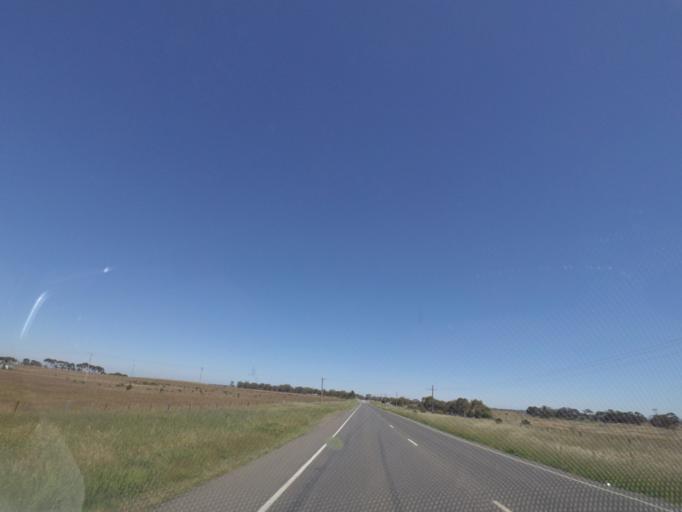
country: AU
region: Victoria
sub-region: Melton
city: Brookfield
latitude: -37.6827
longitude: 144.5035
